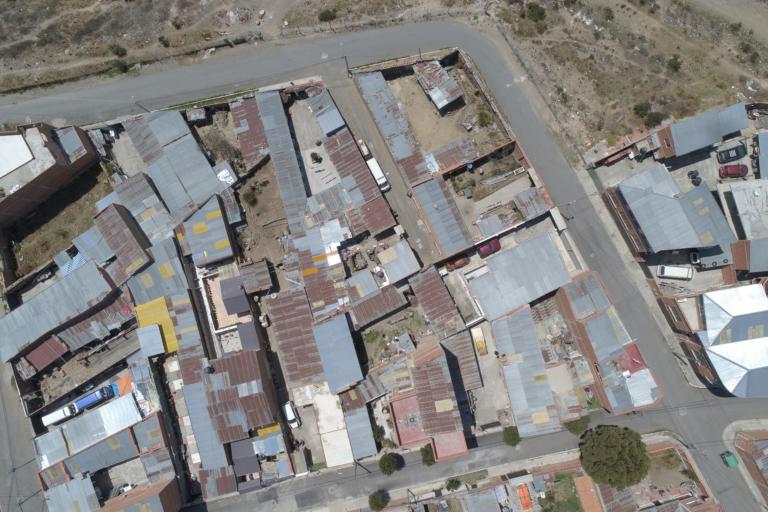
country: BO
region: La Paz
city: La Paz
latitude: -16.5010
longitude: -68.1011
